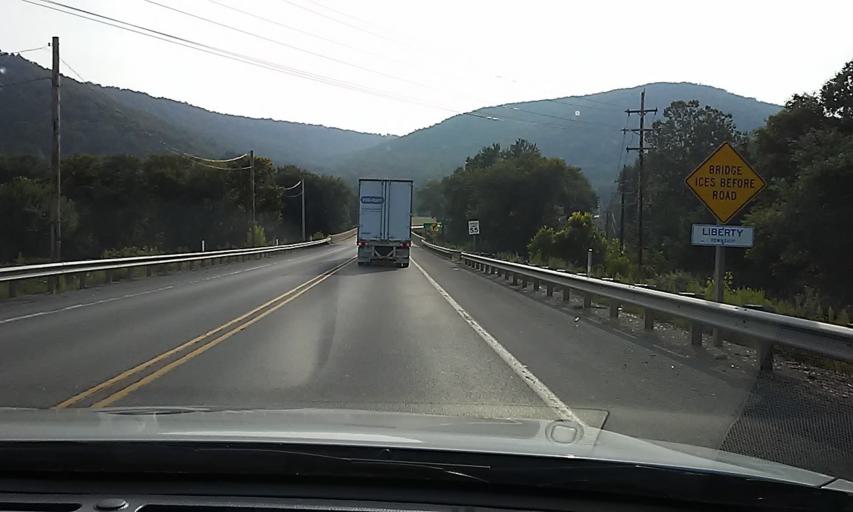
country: US
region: Pennsylvania
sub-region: McKean County
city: Port Allegany
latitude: 41.8190
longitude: -78.2915
